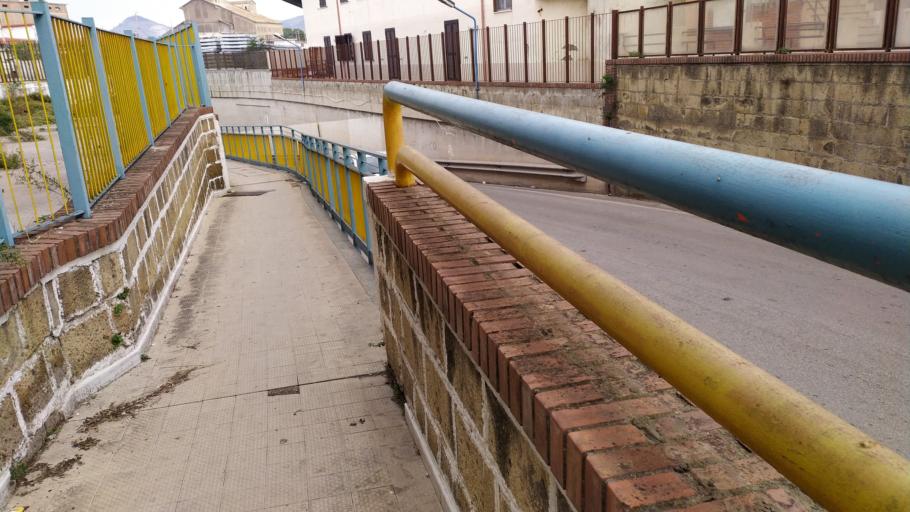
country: IT
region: Campania
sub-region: Provincia di Caserta
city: Montedecoro
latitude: 40.9952
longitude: 14.4208
